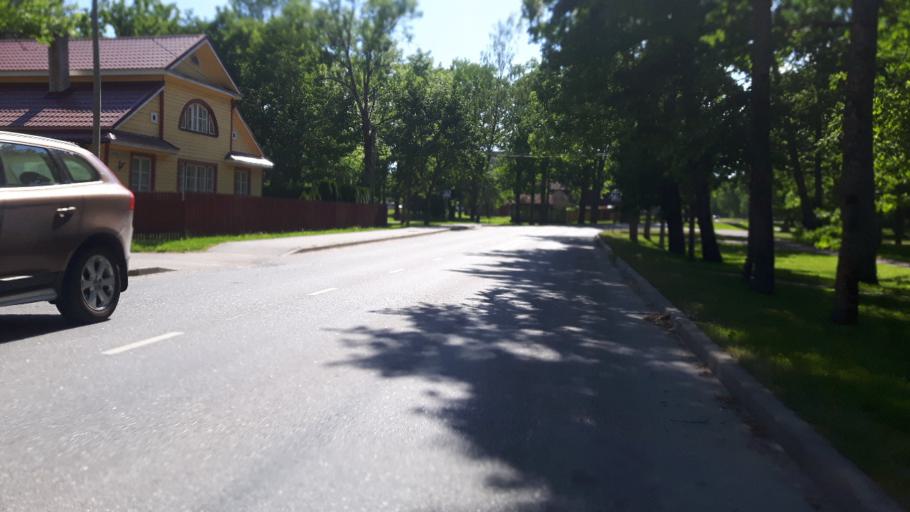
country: EE
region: Paernumaa
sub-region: Sindi linn
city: Sindi
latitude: 58.4076
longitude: 24.6577
